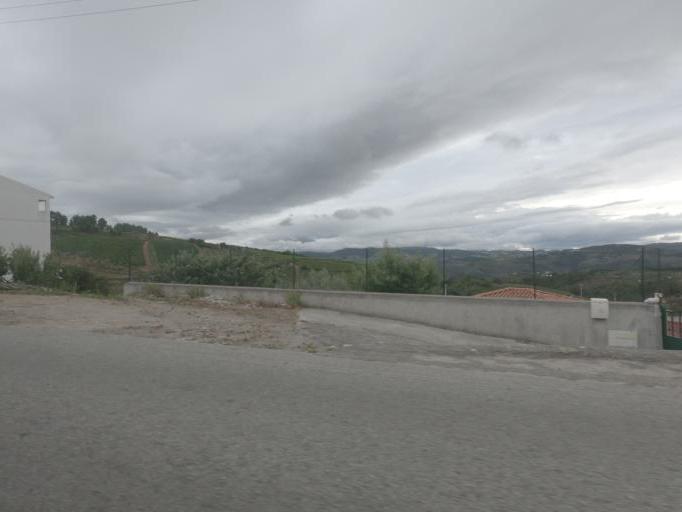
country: PT
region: Vila Real
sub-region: Sabrosa
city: Sabrosa
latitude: 41.2877
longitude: -7.5156
